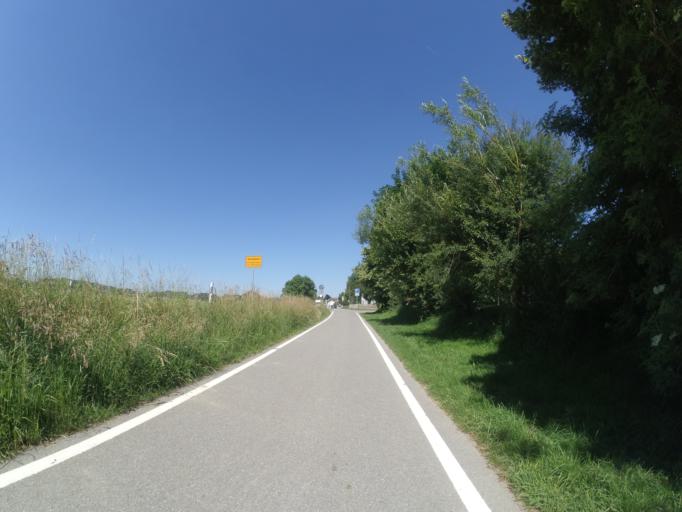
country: DE
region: Baden-Wuerttemberg
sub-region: Tuebingen Region
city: Leutkirch im Allgau
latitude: 47.8450
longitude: 9.9718
